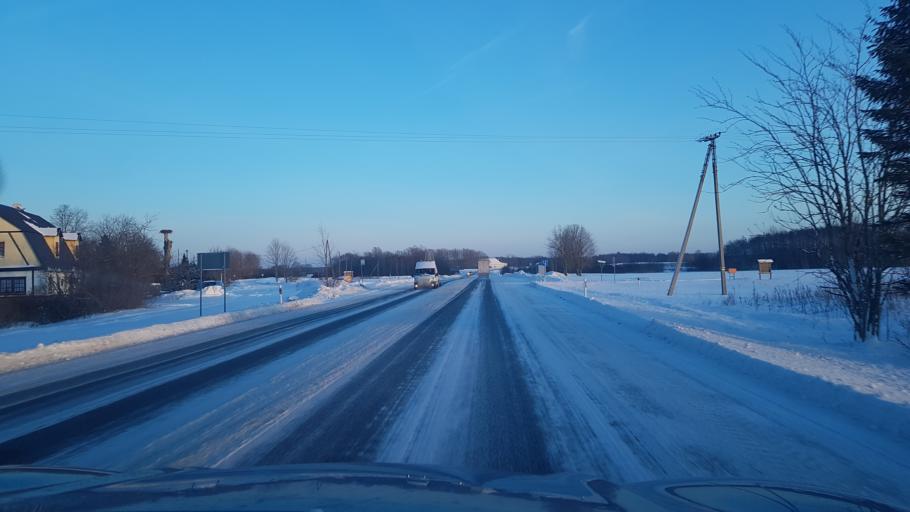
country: EE
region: Ida-Virumaa
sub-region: Narva-Joesuu linn
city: Narva-Joesuu
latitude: 59.4016
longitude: 28.0608
